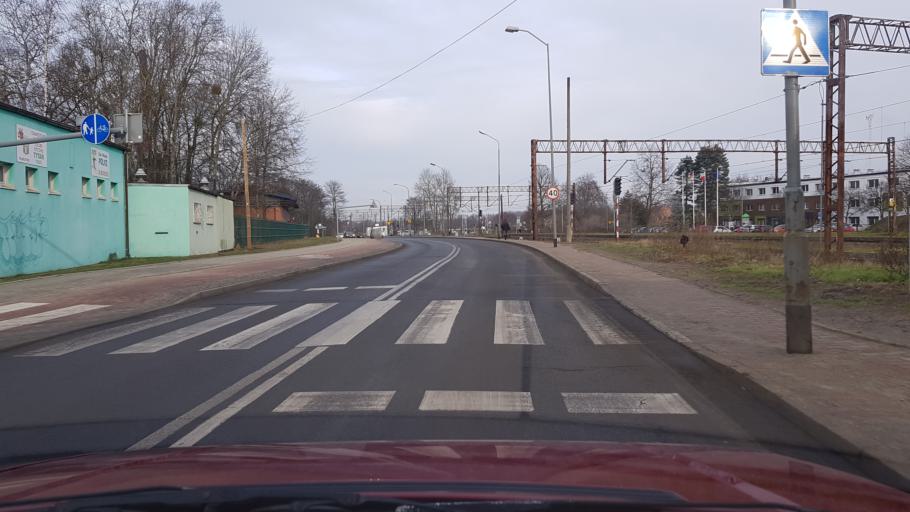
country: PL
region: West Pomeranian Voivodeship
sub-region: Powiat policki
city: Police
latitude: 53.5494
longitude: 14.5653
